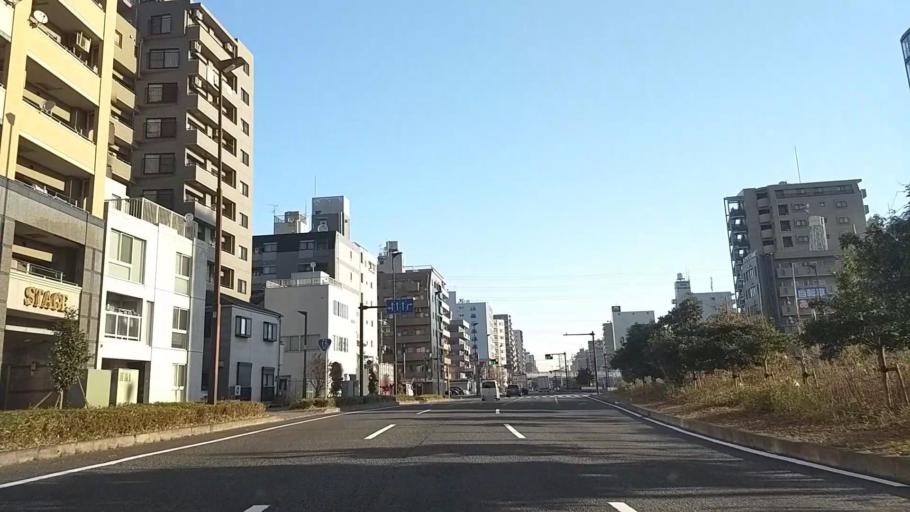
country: JP
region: Kanagawa
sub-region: Kawasaki-shi
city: Kawasaki
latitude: 35.5203
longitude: 139.6904
